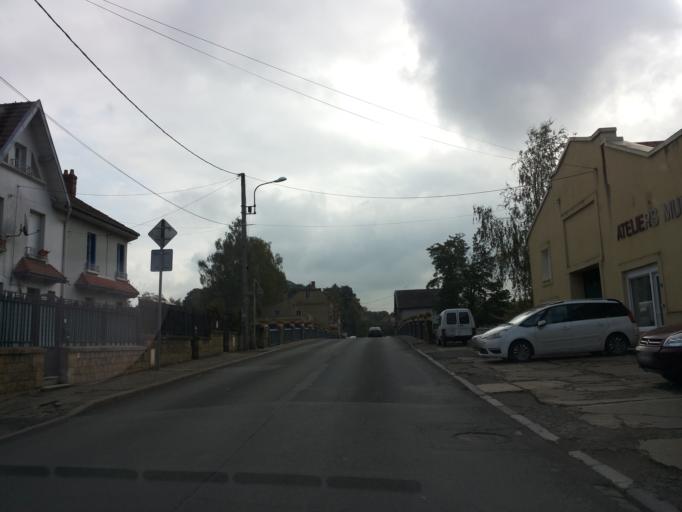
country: FR
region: Lorraine
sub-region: Departement de la Meuse
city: Montmedy
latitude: 49.5166
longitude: 5.3677
